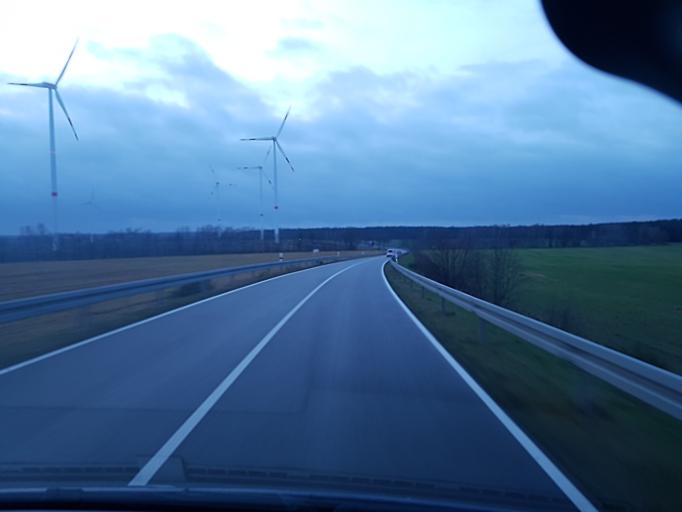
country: DE
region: Brandenburg
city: Bronkow
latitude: 51.6504
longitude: 13.8870
